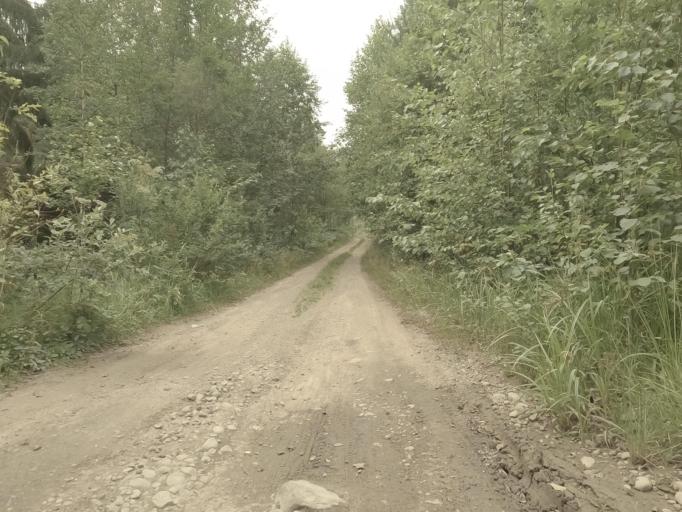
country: RU
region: Leningrad
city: Kamennogorsk
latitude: 61.0106
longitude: 29.1924
